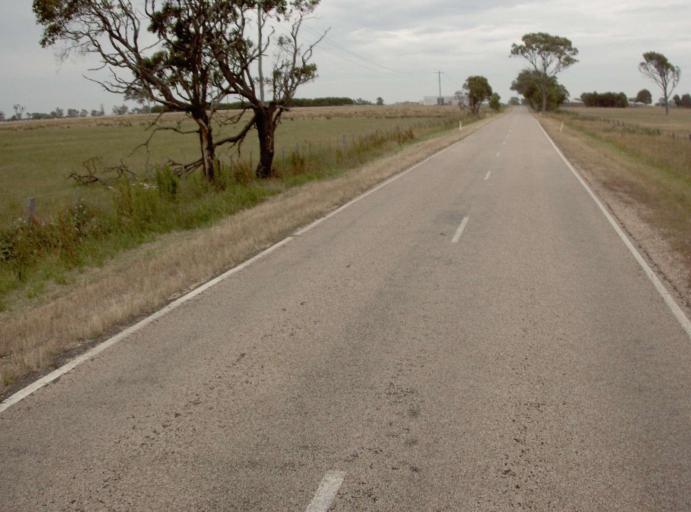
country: AU
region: Victoria
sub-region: East Gippsland
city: Bairnsdale
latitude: -37.8512
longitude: 147.4290
